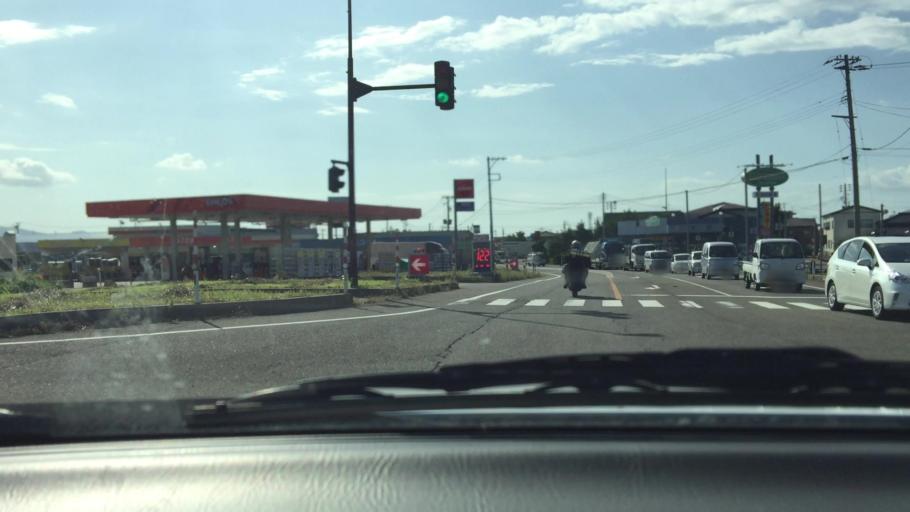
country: JP
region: Niigata
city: Kashiwazaki
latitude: 37.3887
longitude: 138.5909
